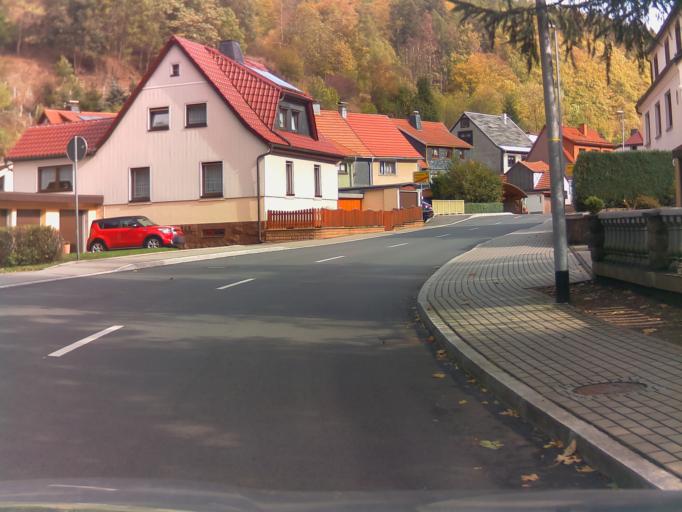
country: DE
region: Thuringia
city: Unterschonau
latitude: 50.7148
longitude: 10.5787
